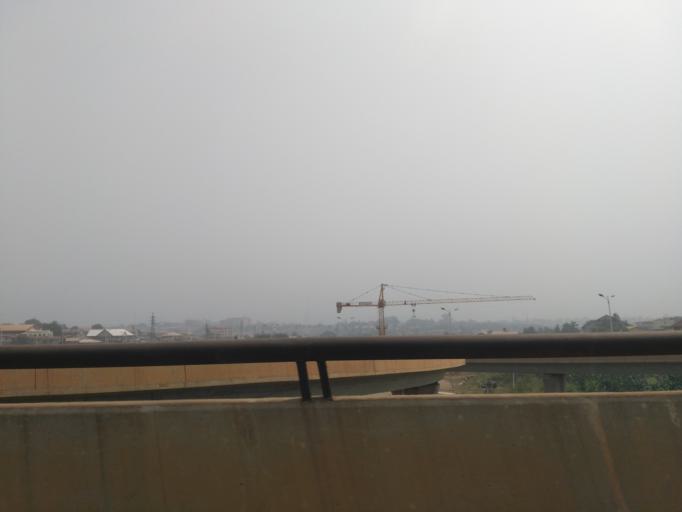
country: GH
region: Ashanti
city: Kumasi
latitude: 6.6990
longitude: -1.6456
